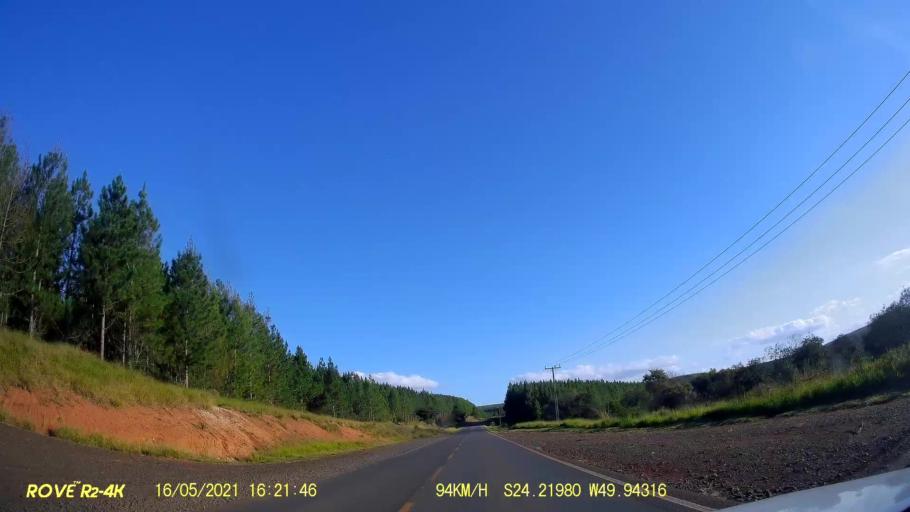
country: BR
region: Parana
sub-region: Jaguariaiva
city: Jaguariaiva
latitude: -24.2199
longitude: -49.9432
